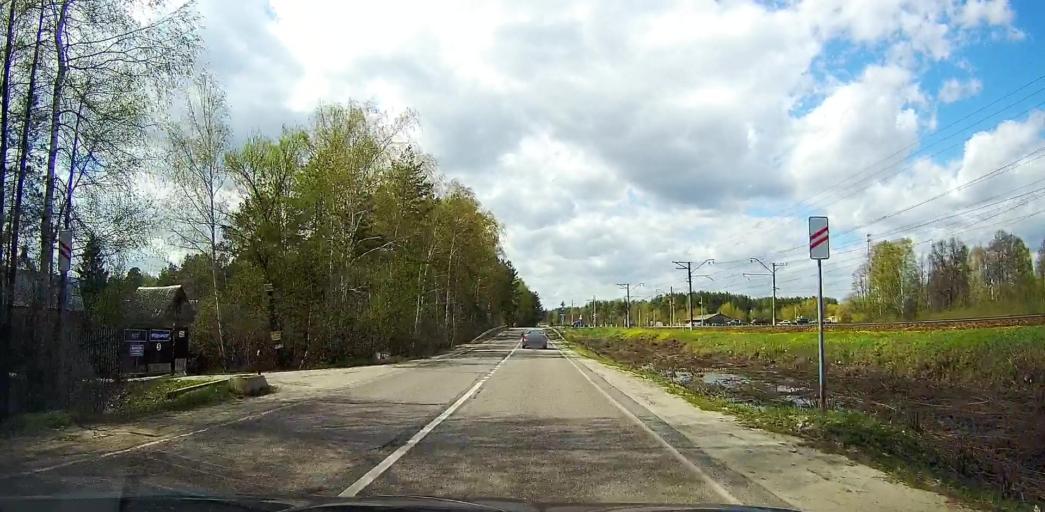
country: RU
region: Moskovskaya
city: Davydovo
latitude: 55.5723
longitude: 38.8210
